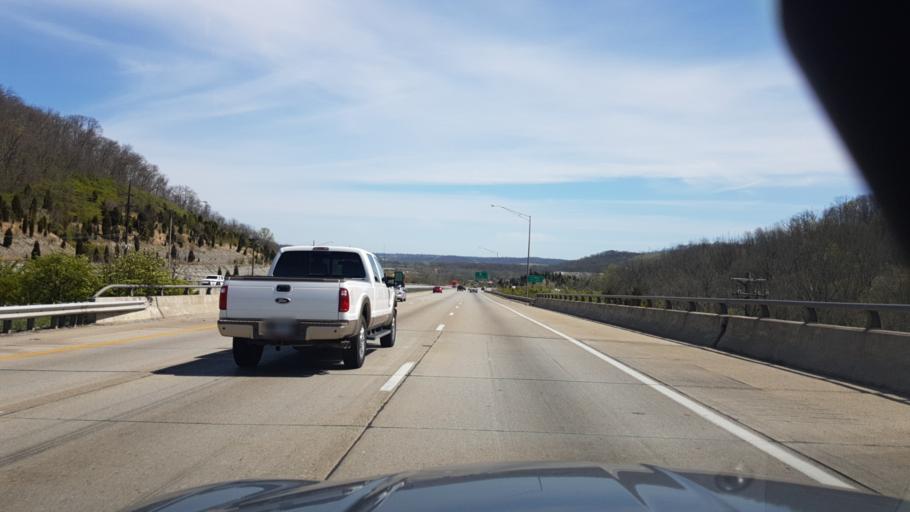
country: US
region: Kentucky
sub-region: Kenton County
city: Lakeside Park
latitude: 39.0267
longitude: -84.5451
